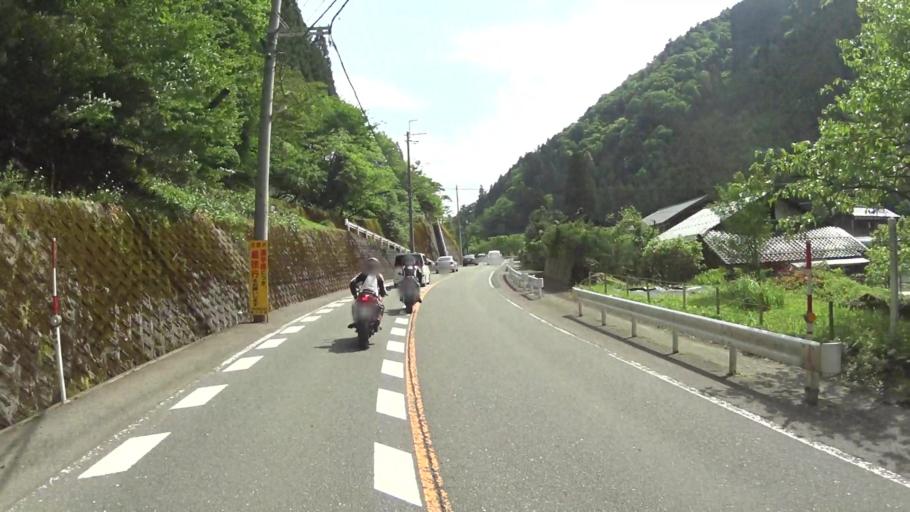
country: JP
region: Shiga Prefecture
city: Kitahama
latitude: 35.2756
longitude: 135.8782
